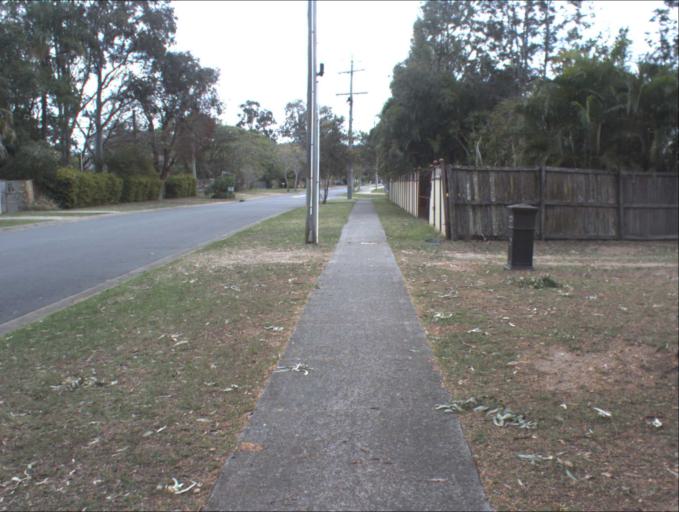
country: AU
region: Queensland
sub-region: Logan
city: Waterford West
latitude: -27.7004
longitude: 153.1357
